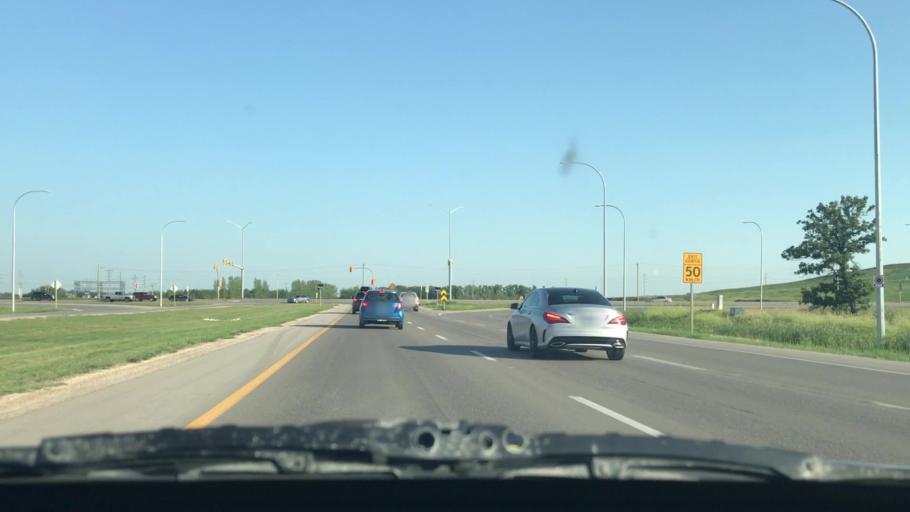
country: CA
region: Manitoba
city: Winnipeg
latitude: 49.7707
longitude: -97.1842
